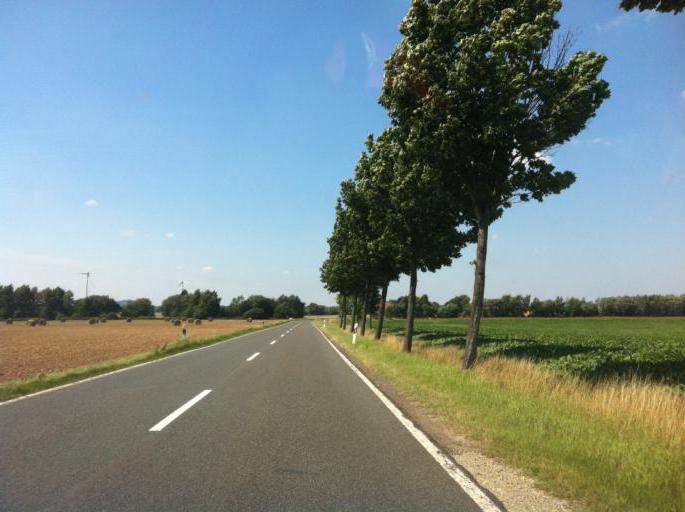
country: DE
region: Thuringia
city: Siemerode
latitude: 51.4283
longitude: 10.0854
